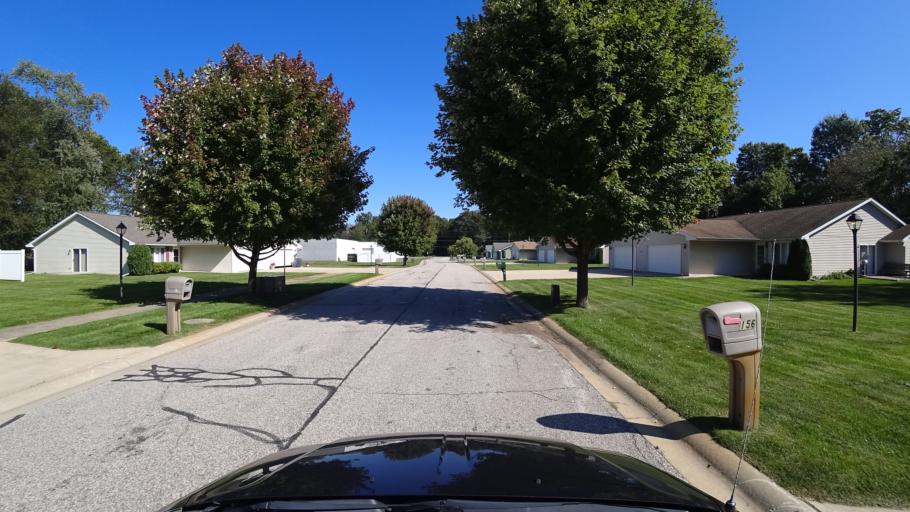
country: US
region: Indiana
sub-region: LaPorte County
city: Michigan City
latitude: 41.6871
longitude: -86.9059
